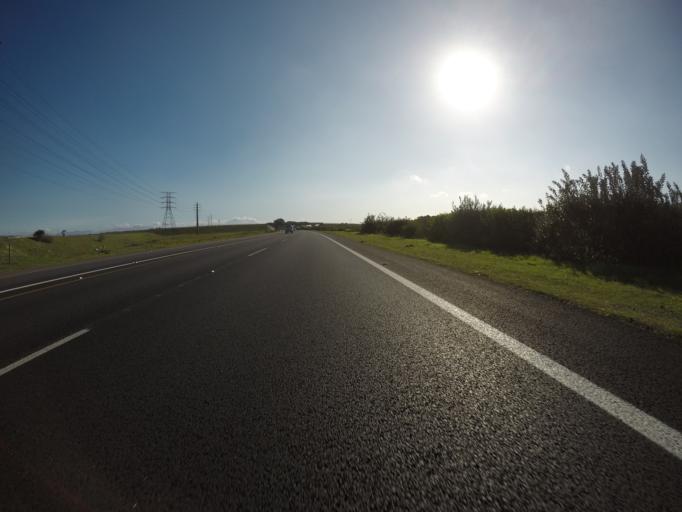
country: ZA
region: Western Cape
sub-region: Cape Winelands District Municipality
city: Stellenbosch
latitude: -34.0465
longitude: 18.7533
